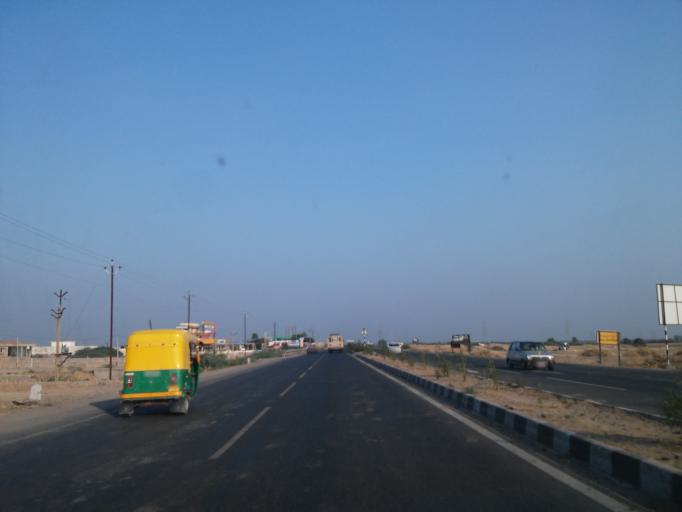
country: IN
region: Gujarat
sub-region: Ahmadabad
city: Mandal
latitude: 23.0981
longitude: 72.0684
